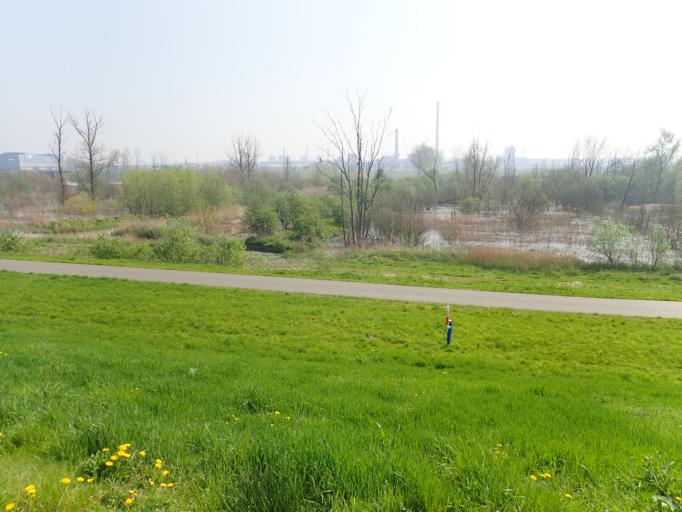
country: BE
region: Flanders
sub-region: Provincie Oost-Vlaanderen
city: Kruibeke
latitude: 51.1687
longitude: 4.3169
